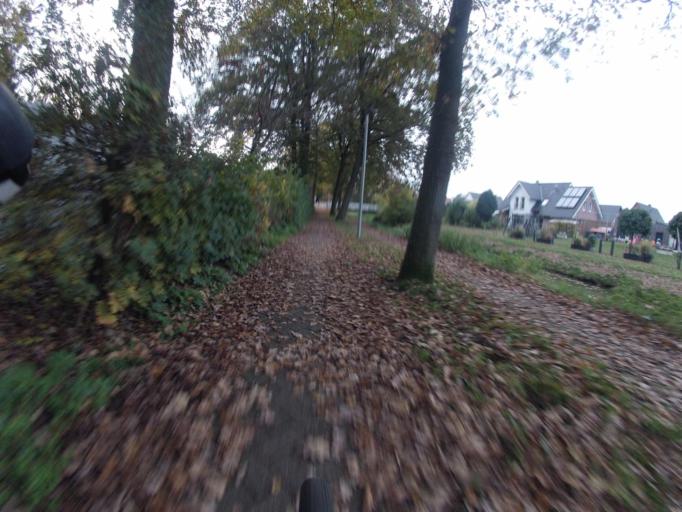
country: DE
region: North Rhine-Westphalia
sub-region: Regierungsbezirk Munster
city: Horstel
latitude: 52.2720
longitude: 7.5766
